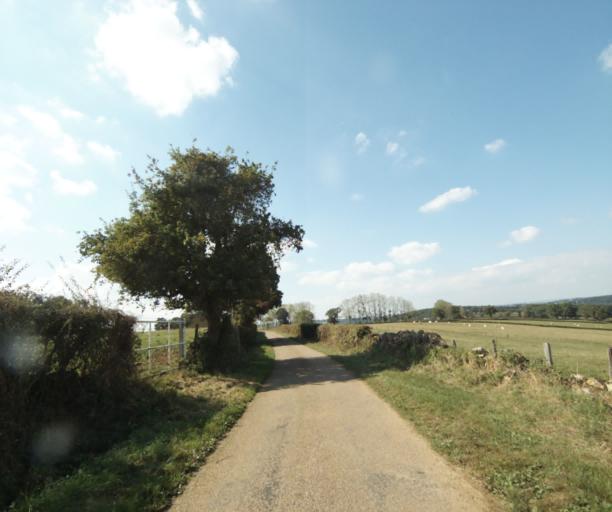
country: FR
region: Bourgogne
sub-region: Departement de Saone-et-Loire
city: Charolles
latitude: 46.3830
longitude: 4.2272
